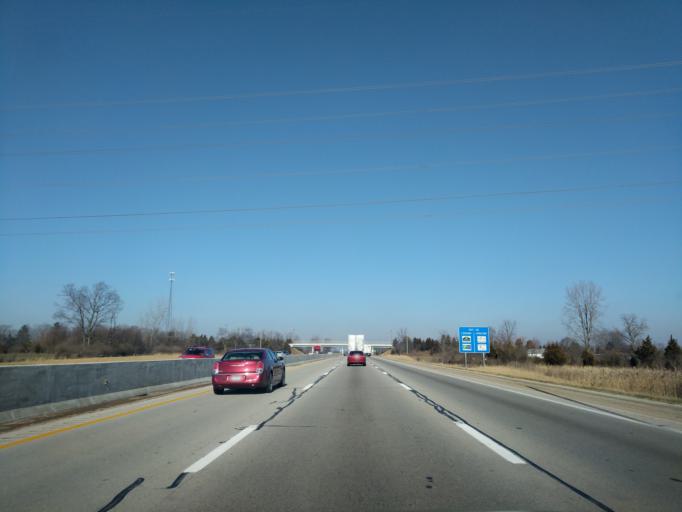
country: US
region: Ohio
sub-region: Miami County
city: Tipp City
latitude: 39.9419
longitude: -84.1889
